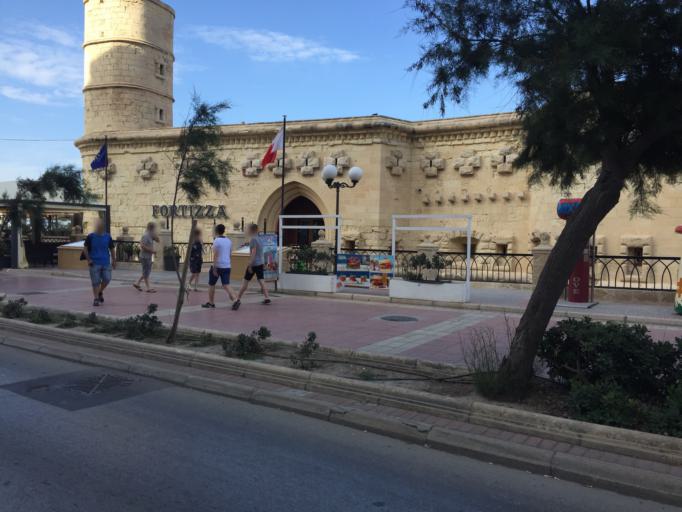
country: MT
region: Tas-Sliema
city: Sliema
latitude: 35.9140
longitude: 14.5067
